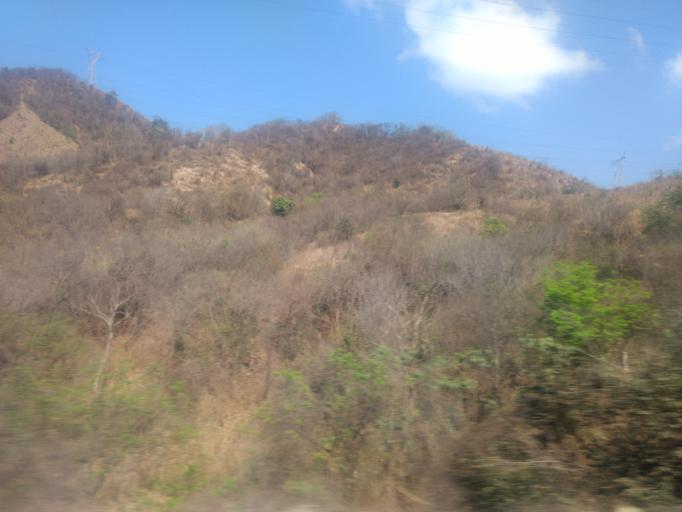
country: MX
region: Colima
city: El Colomo
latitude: 19.0583
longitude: -104.2698
